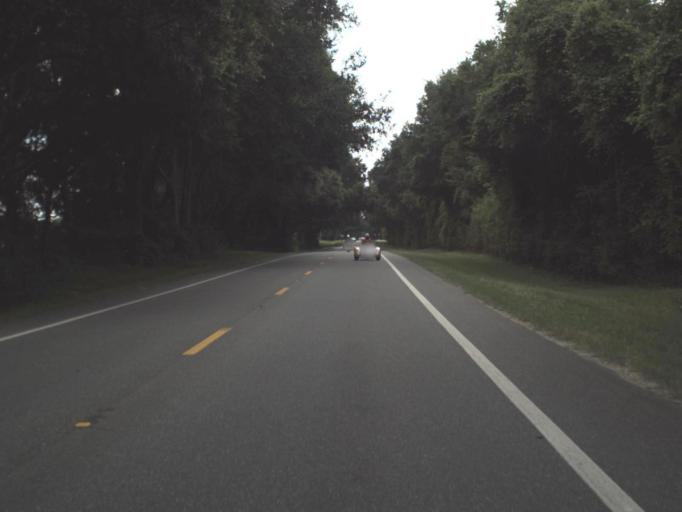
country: US
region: Florida
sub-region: Alachua County
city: Newberry
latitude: 29.6134
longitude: -82.5904
